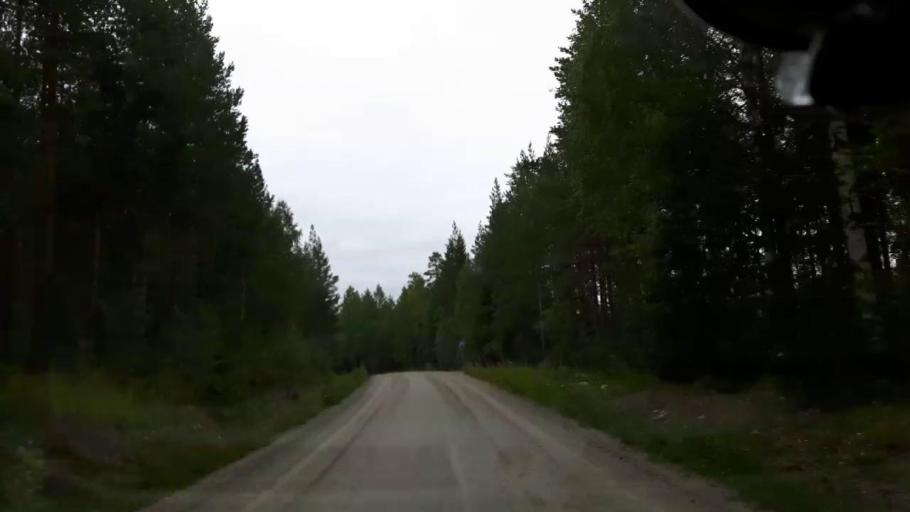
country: SE
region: Jaemtland
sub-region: Braecke Kommun
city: Braecke
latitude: 62.8287
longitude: 15.6947
